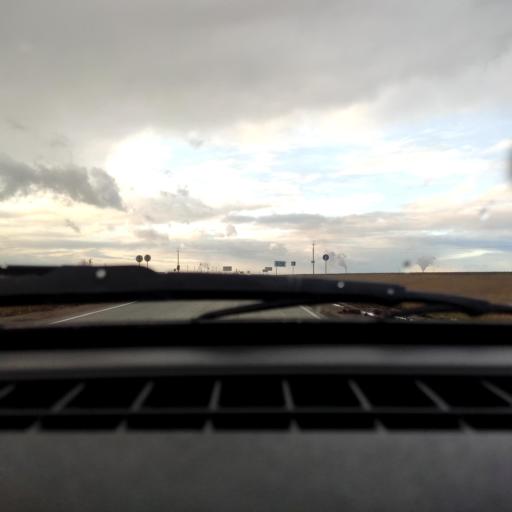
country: RU
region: Bashkortostan
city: Iglino
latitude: 54.7462
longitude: 56.2989
